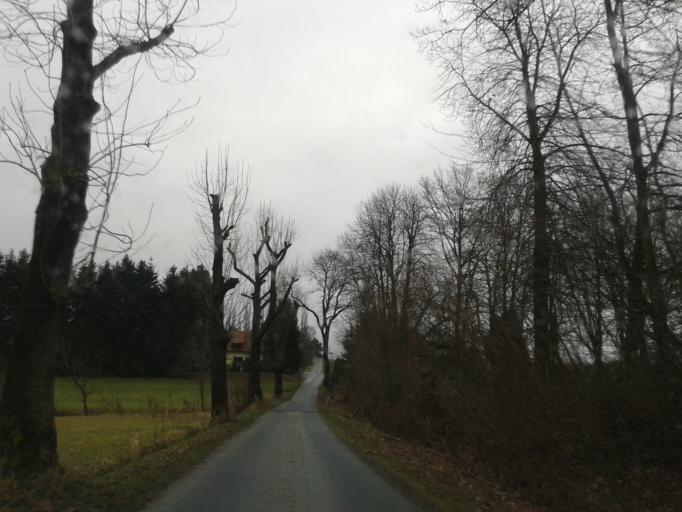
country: DE
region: Saxony
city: Neugersdorf
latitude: 50.9735
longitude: 14.6224
